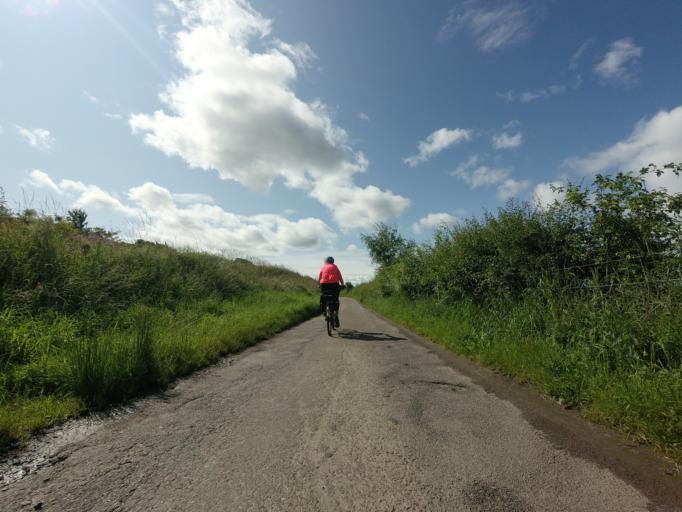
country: GB
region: Scotland
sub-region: Moray
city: Kinloss
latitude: 57.6420
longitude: -3.5214
